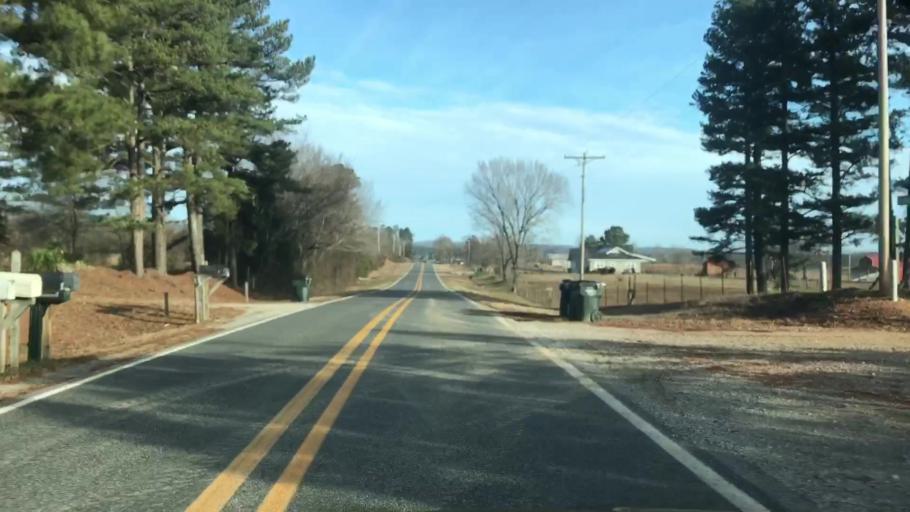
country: US
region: Arkansas
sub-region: Garland County
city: Rockwell
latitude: 34.4976
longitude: -93.2765
